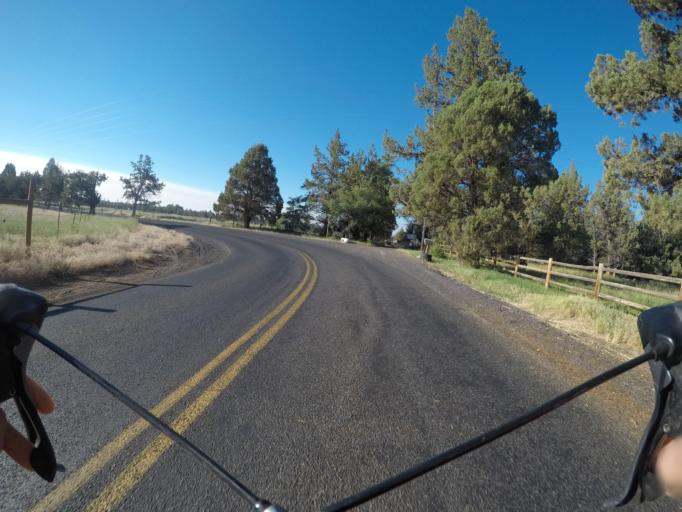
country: US
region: Oregon
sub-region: Deschutes County
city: Redmond
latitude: 44.2624
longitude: -121.2451
